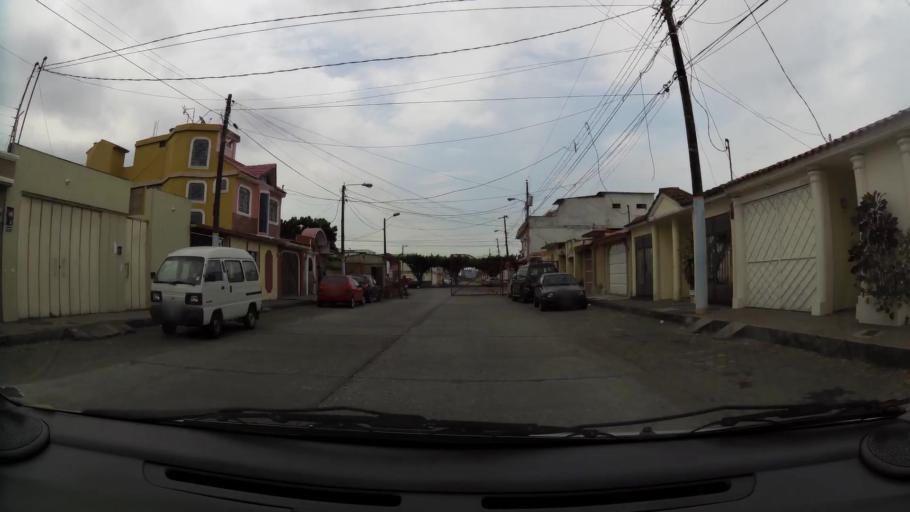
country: EC
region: Guayas
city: Eloy Alfaro
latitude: -2.1141
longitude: -79.8955
